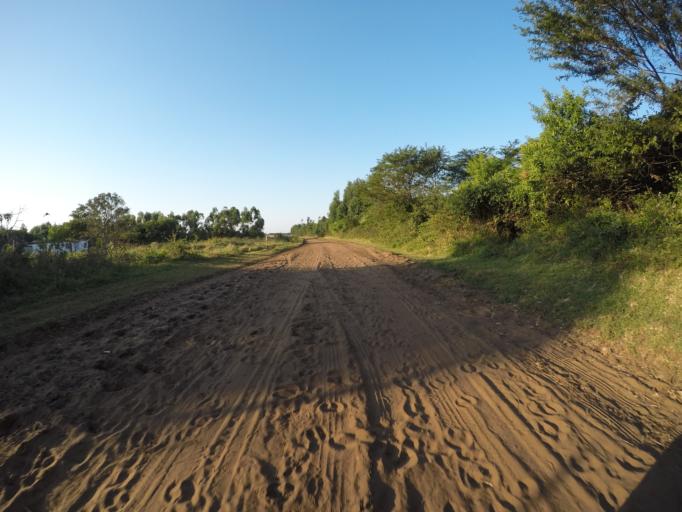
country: ZA
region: KwaZulu-Natal
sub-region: uThungulu District Municipality
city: KwaMbonambi
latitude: -28.6910
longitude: 32.2036
